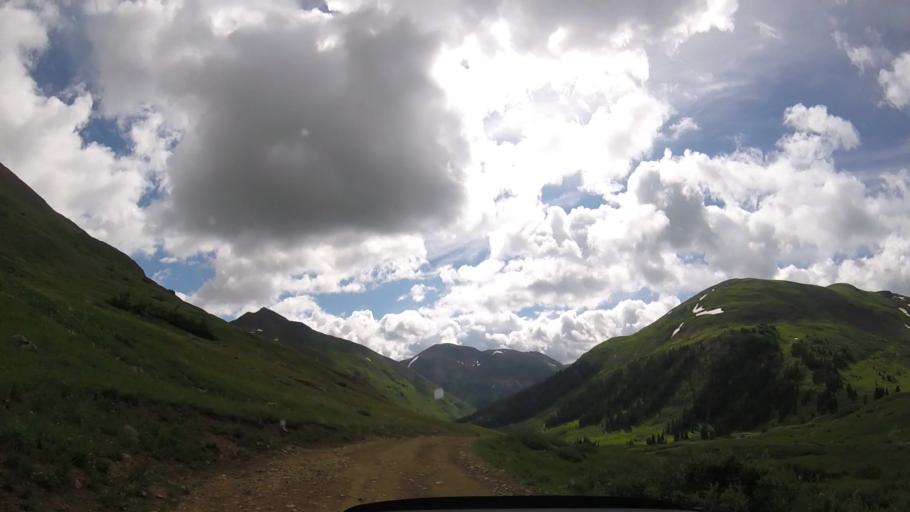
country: US
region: Colorado
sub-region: Ouray County
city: Ouray
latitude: 37.9322
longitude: -107.5918
